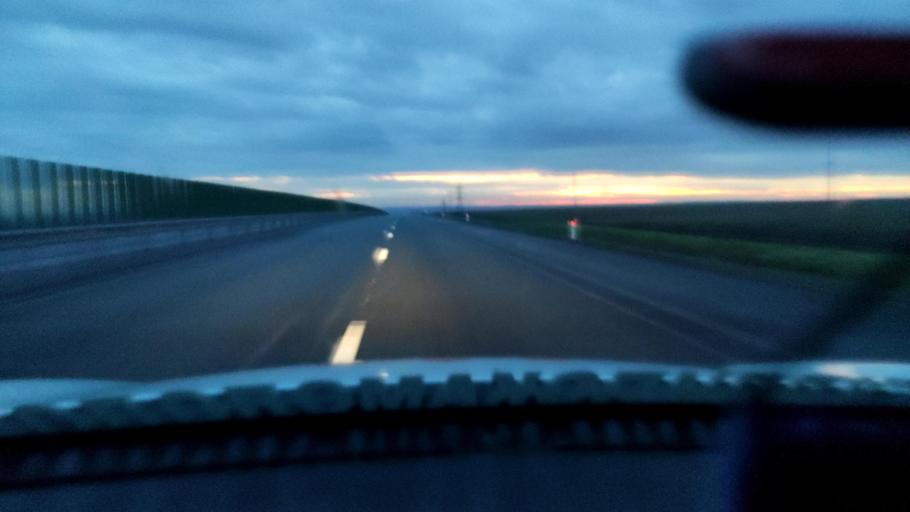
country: RU
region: Rostov
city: Tarasovskiy
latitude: 48.6720
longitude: 40.3696
